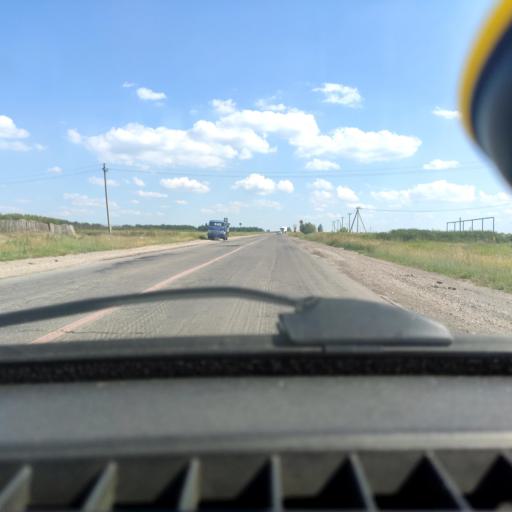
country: RU
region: Samara
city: Povolzhskiy
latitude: 53.7507
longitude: 49.7424
